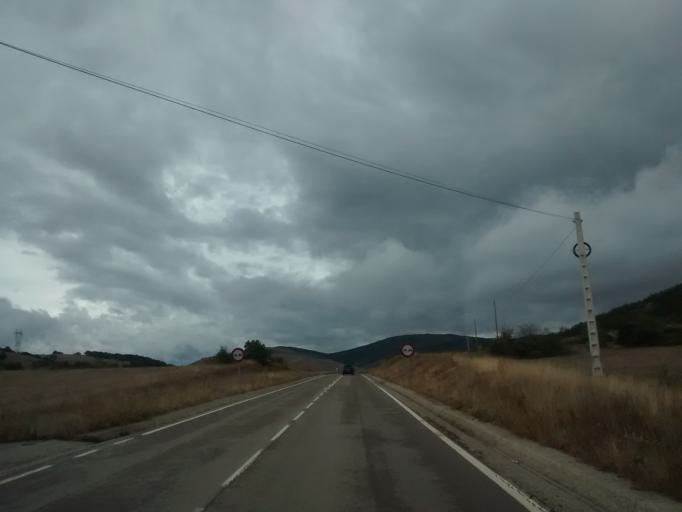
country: ES
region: Cantabria
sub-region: Provincia de Cantabria
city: Mataporquera
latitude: 42.8877
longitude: -4.0745
